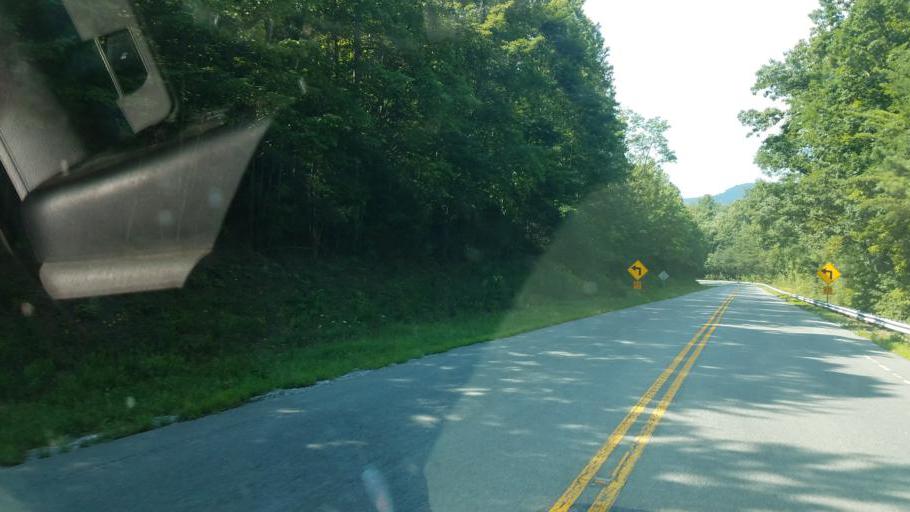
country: US
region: North Carolina
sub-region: Avery County
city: Newland
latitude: 35.9254
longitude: -81.8196
